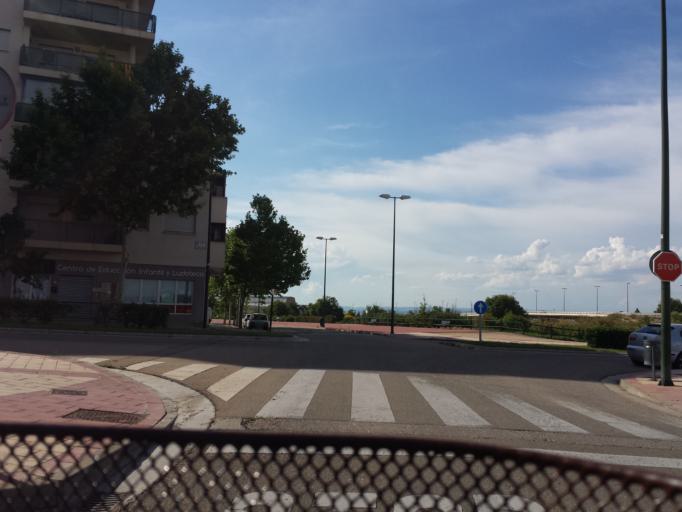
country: ES
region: Aragon
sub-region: Provincia de Zaragoza
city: Montecanal
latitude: 41.6387
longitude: -0.9448
